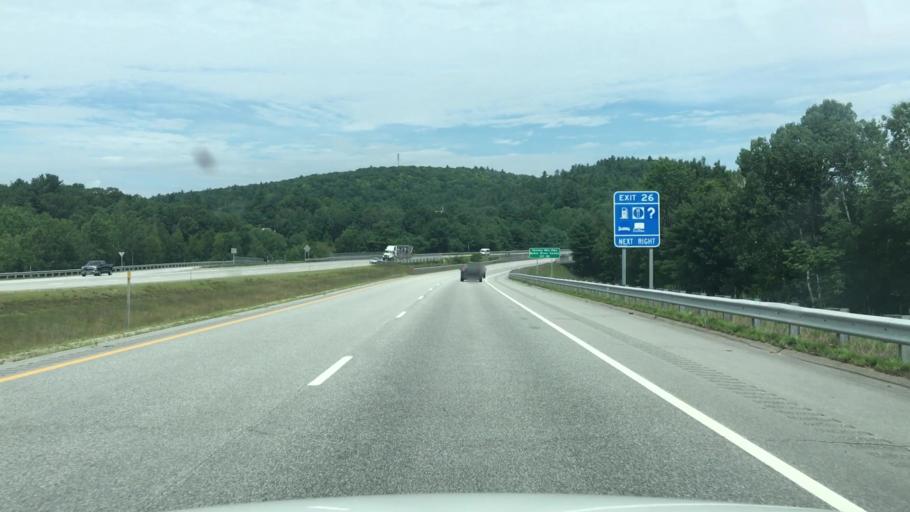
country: US
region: New Hampshire
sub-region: Grafton County
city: Plymouth
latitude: 43.7687
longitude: -71.6818
